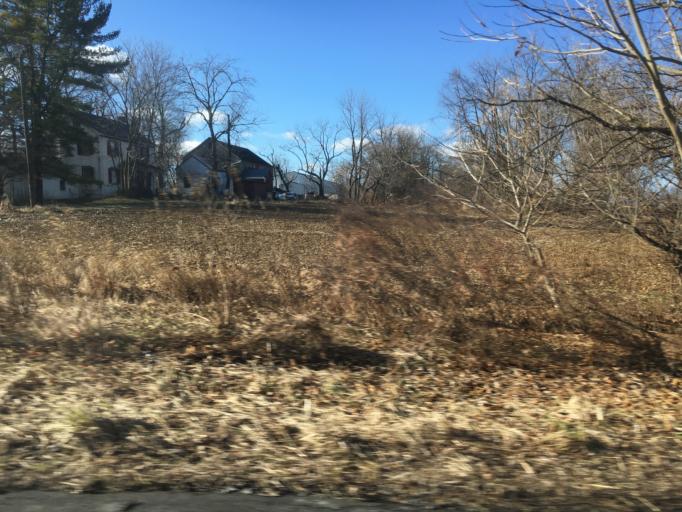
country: US
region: Pennsylvania
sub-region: Lehigh County
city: Stiles
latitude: 40.6267
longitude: -75.5369
